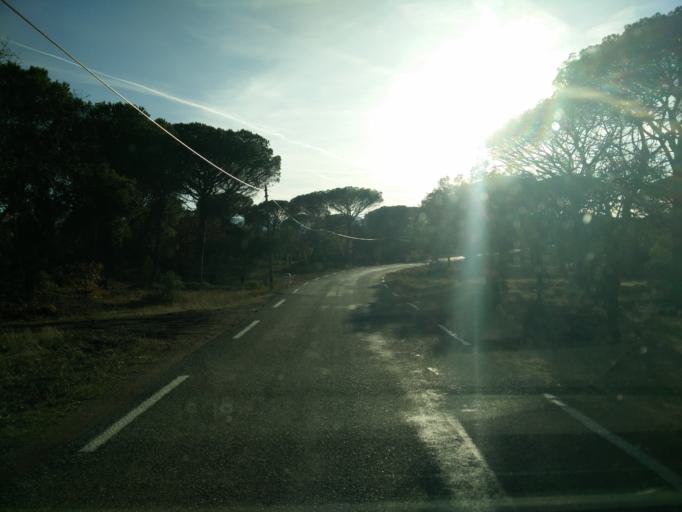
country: FR
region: Provence-Alpes-Cote d'Azur
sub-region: Departement du Var
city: La Garde-Freinet
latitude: 43.3607
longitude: 6.4442
